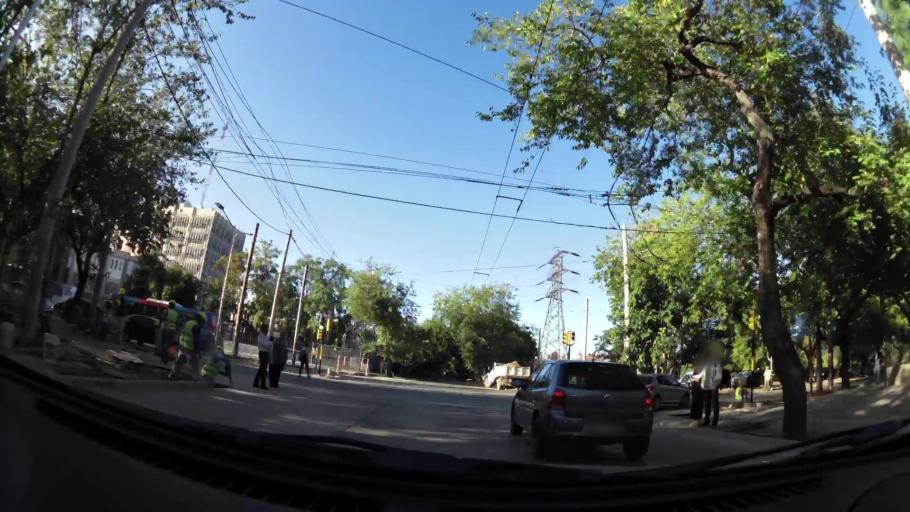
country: AR
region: Mendoza
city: Mendoza
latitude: -32.8991
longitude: -68.8430
